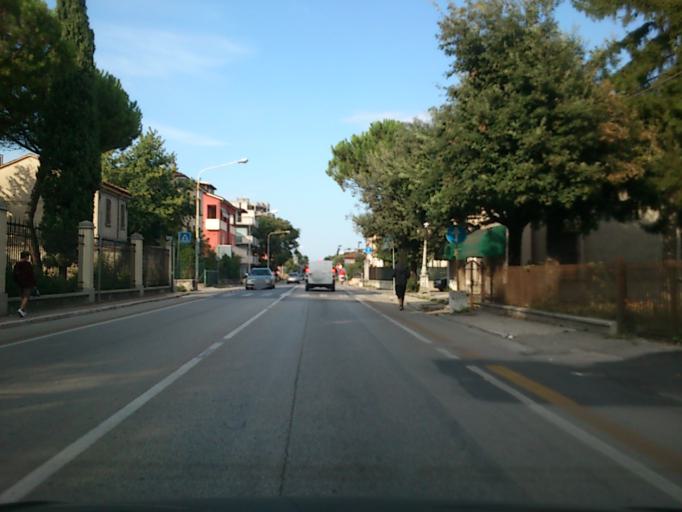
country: IT
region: The Marches
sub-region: Provincia di Pesaro e Urbino
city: Fano
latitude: 43.8380
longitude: 13.0083
